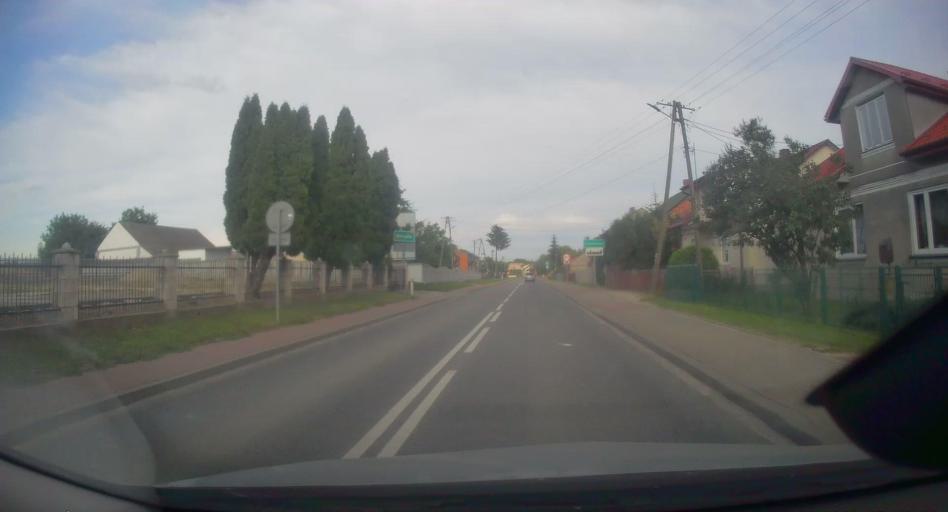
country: PL
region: Lesser Poland Voivodeship
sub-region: Powiat brzeski
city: Szczurowa
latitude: 50.1648
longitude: 20.5815
